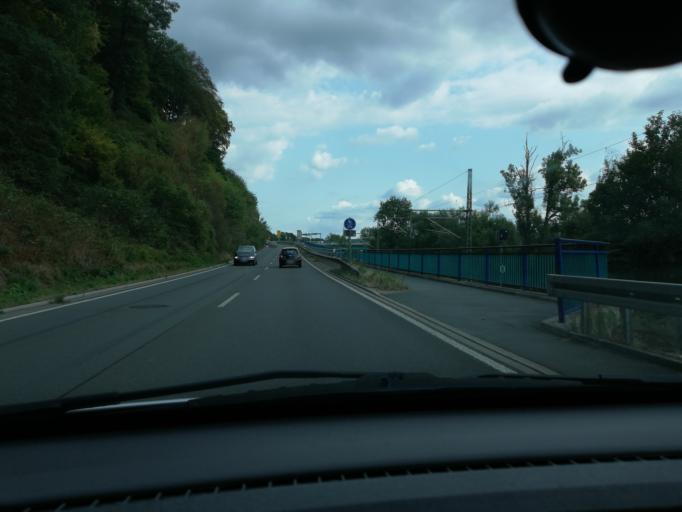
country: DE
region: North Rhine-Westphalia
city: Wetter (Ruhr)
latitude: 51.3925
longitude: 7.3758
